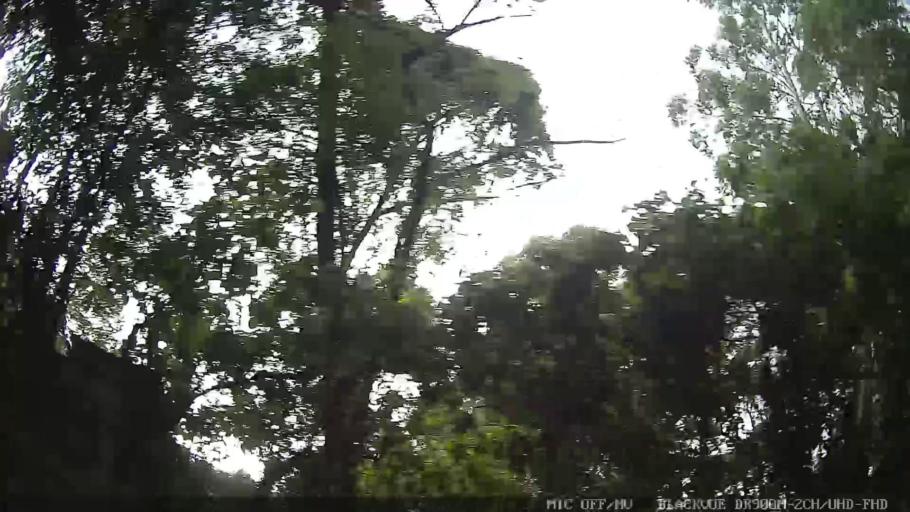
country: BR
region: Sao Paulo
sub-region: Osasco
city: Osasco
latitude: -23.4653
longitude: -46.7125
